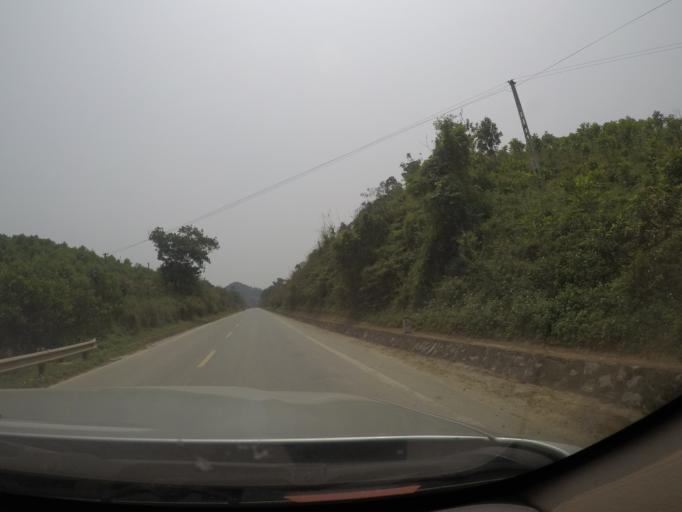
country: VN
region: Thanh Hoa
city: Thi Tran Yen Cat
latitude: 19.6849
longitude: 105.4552
